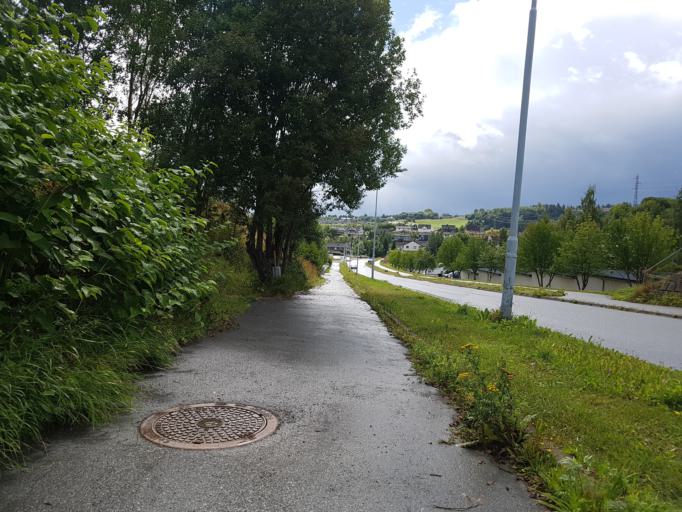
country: NO
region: Sor-Trondelag
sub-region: Trondheim
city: Trondheim
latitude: 63.3904
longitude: 10.3538
